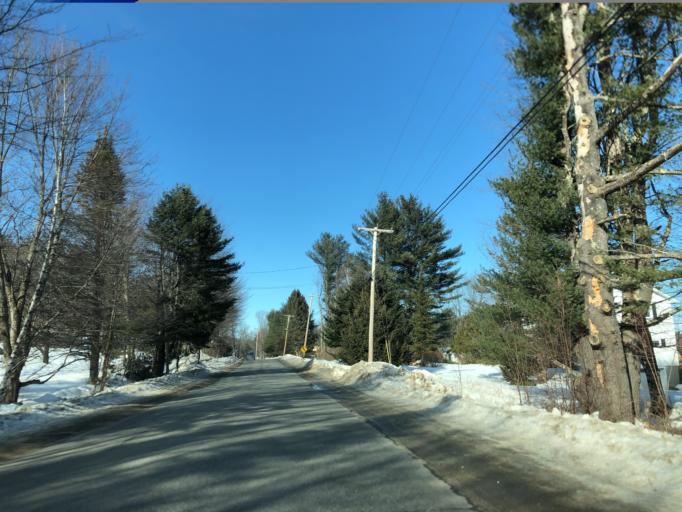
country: US
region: Maine
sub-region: Oxford County
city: Buckfield
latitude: 44.2812
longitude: -70.3571
